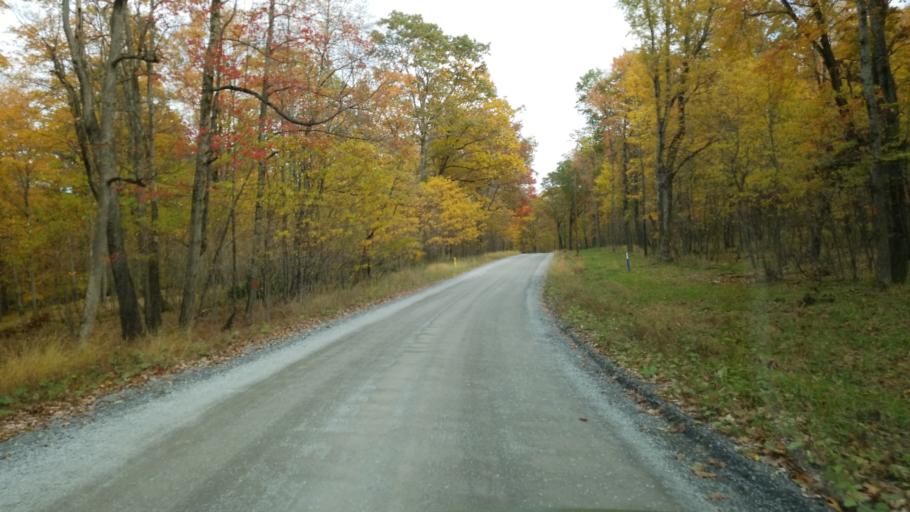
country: US
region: Pennsylvania
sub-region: Clearfield County
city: Clearfield
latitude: 41.1635
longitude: -78.4498
